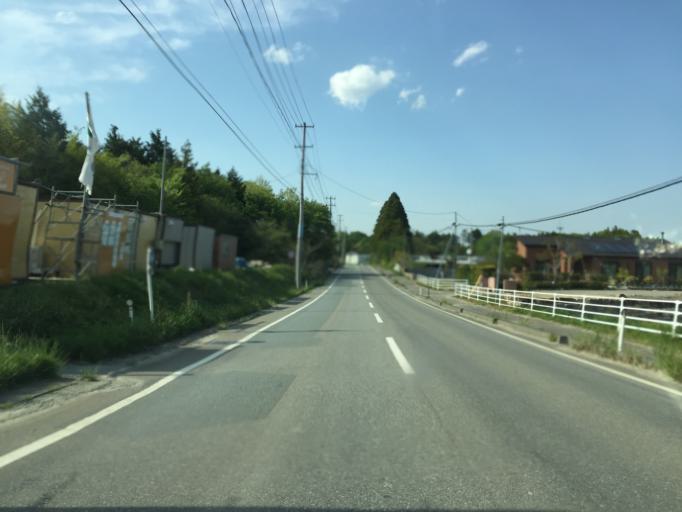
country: JP
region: Fukushima
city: Namie
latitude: 37.3747
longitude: 140.9587
